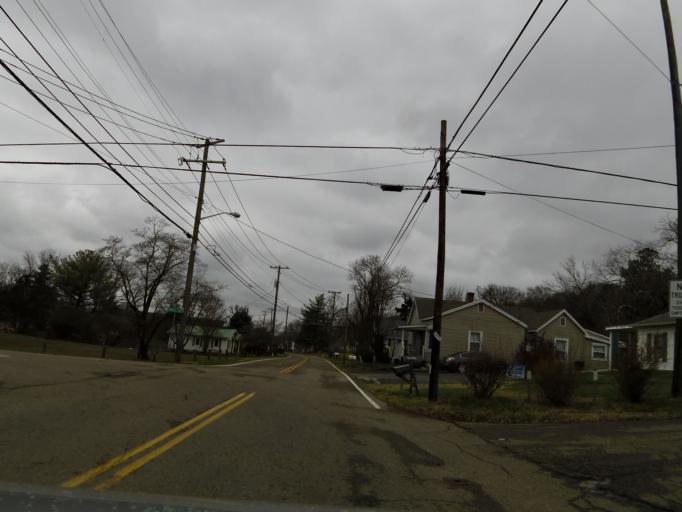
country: US
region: Tennessee
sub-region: Knox County
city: Knoxville
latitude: 35.9657
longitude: -83.9663
